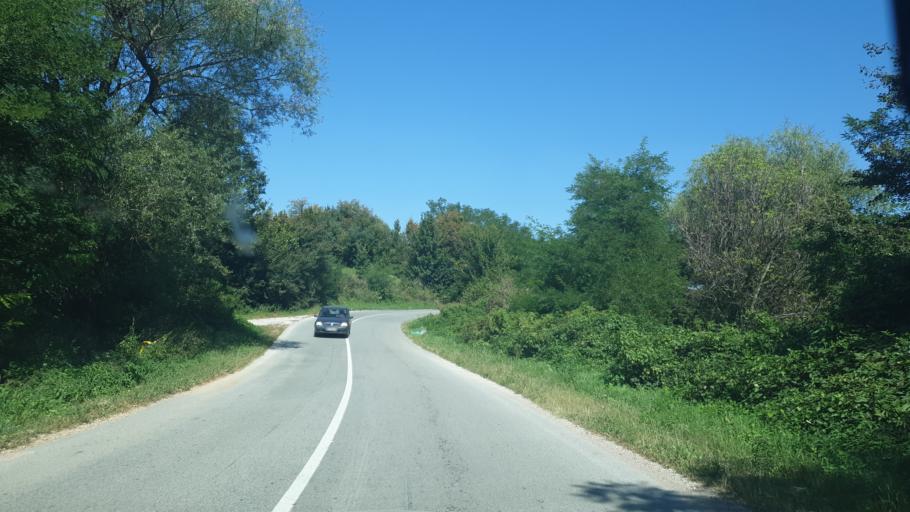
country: RS
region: Central Serbia
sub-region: Kolubarski Okrug
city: Mionica
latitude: 44.1865
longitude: 20.0347
